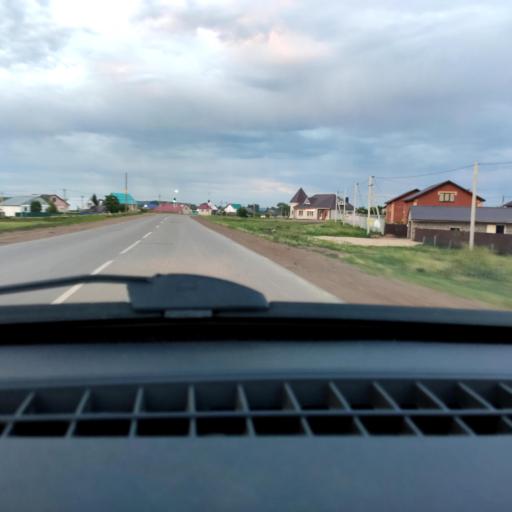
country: RU
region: Bashkortostan
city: Kabakovo
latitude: 54.5477
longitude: 56.0928
